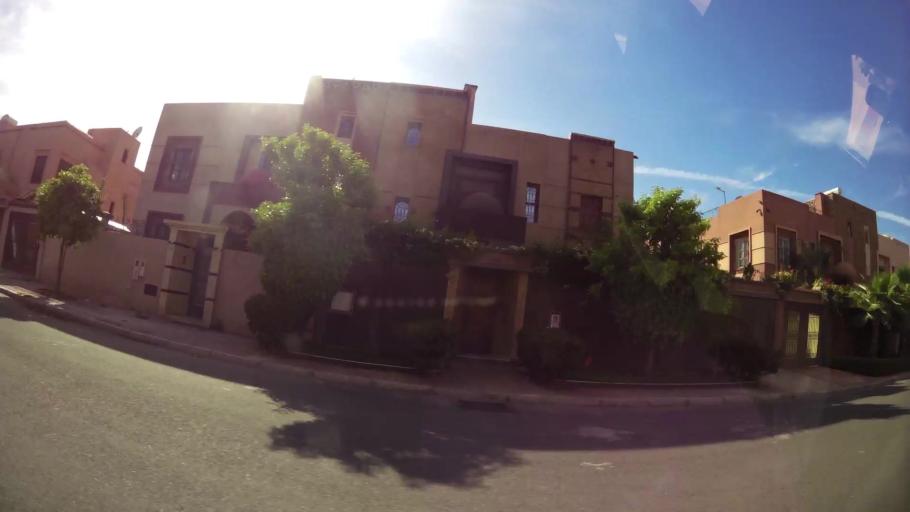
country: MA
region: Marrakech-Tensift-Al Haouz
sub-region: Marrakech
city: Marrakesh
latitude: 31.6521
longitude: -8.0411
